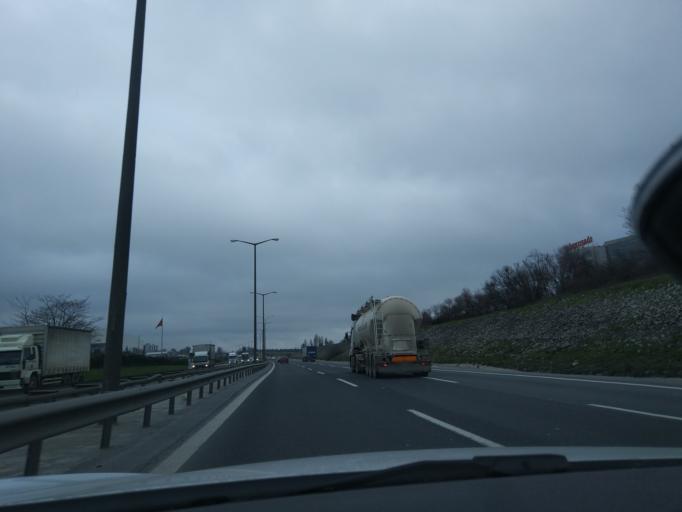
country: TR
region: Istanbul
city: Esenyurt
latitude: 41.0712
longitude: 28.6489
